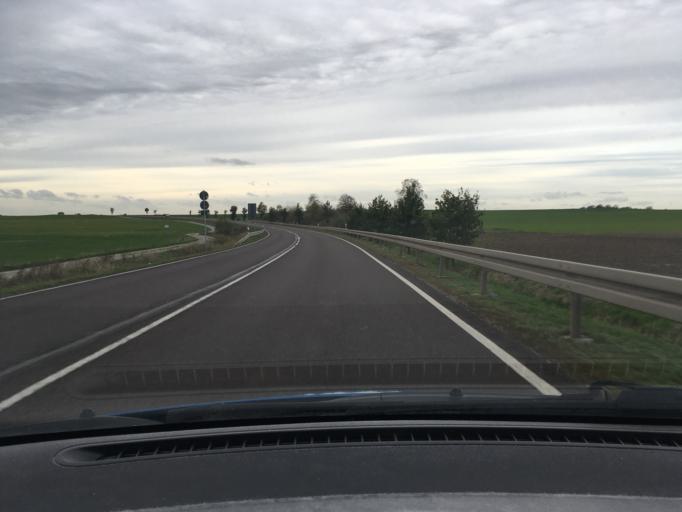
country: DE
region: Saxony-Anhalt
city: Leitzkau
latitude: 52.0595
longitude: 11.9345
